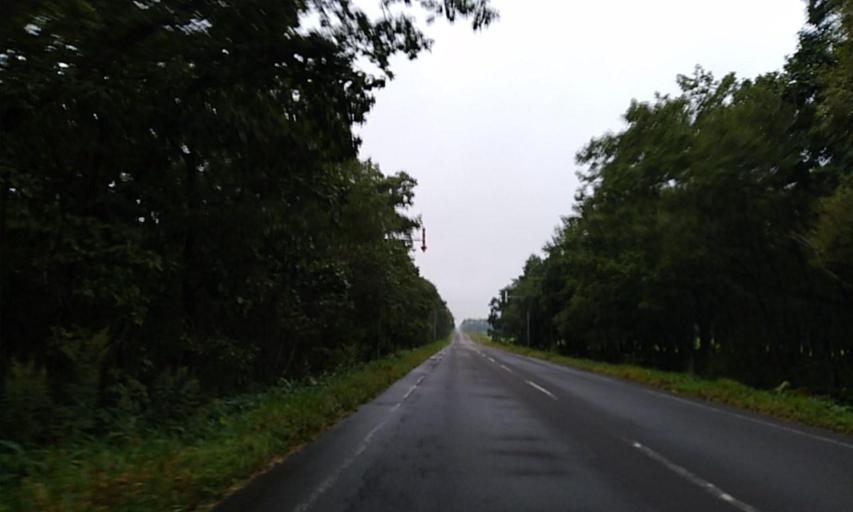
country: JP
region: Hokkaido
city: Shibetsu
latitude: 43.5190
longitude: 144.6829
